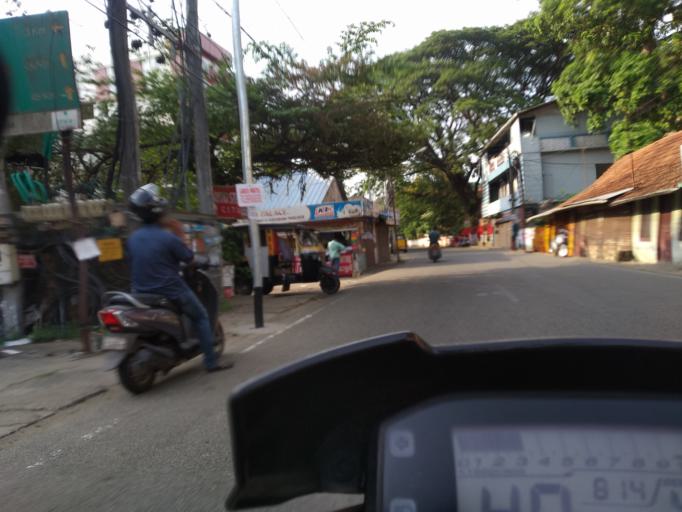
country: IN
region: Kerala
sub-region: Alappuzha
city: Arukutti
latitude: 9.9487
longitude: 76.3474
